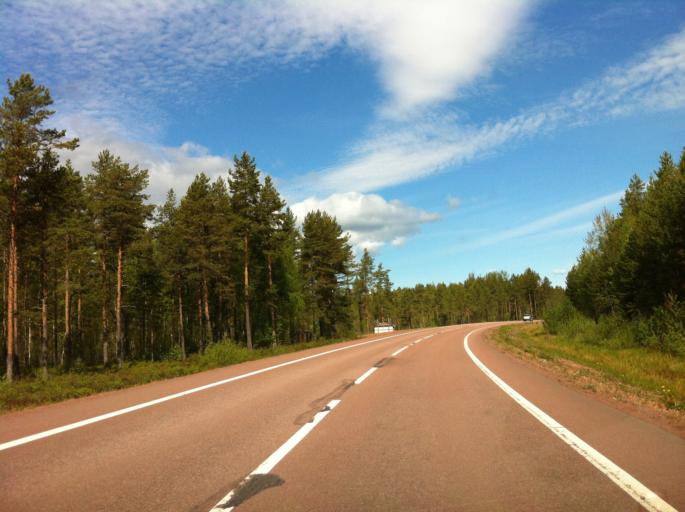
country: SE
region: Dalarna
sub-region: Mora Kommun
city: Mora
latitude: 60.9259
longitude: 14.5696
